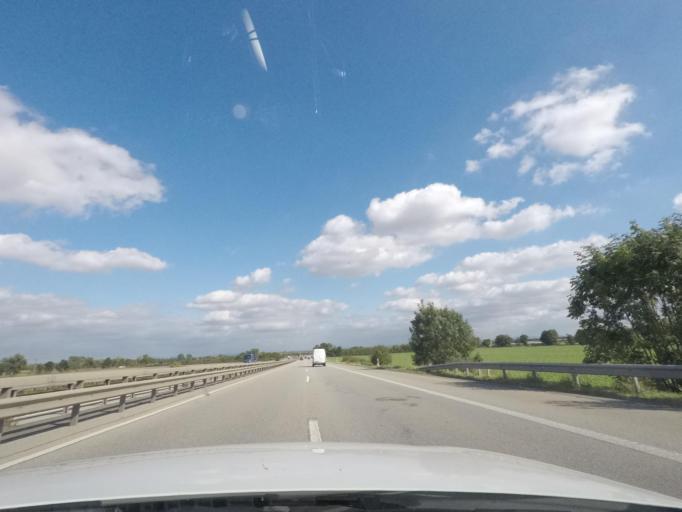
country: DE
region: Rheinland-Pfalz
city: Gerolsheim
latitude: 49.5533
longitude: 8.2659
